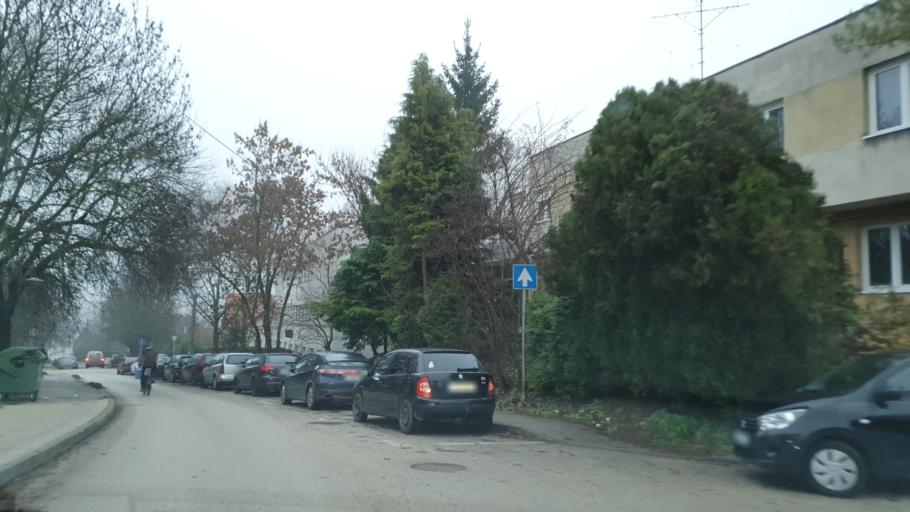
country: HU
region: Veszprem
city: Veszprem
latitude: 47.0816
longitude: 17.9086
